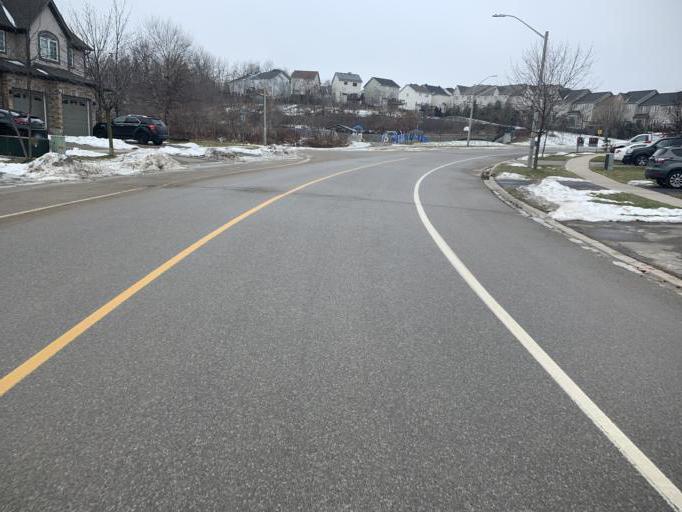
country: CA
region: Ontario
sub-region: Halton
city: Milton
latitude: 43.6604
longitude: -79.9198
